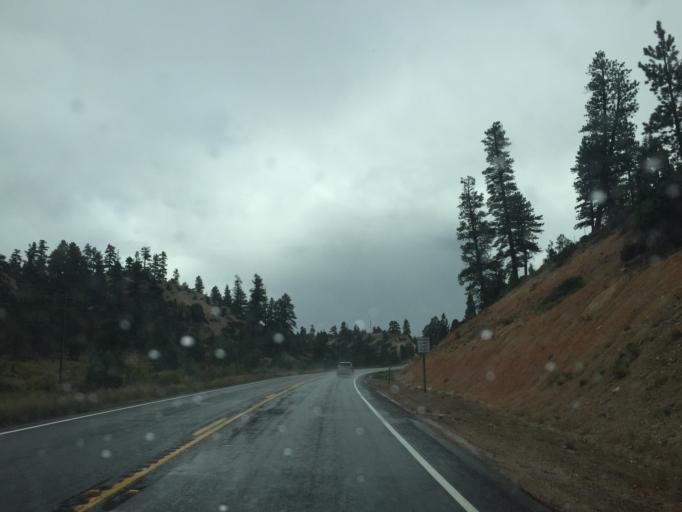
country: US
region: Utah
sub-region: Garfield County
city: Panguitch
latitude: 37.4688
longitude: -112.5172
